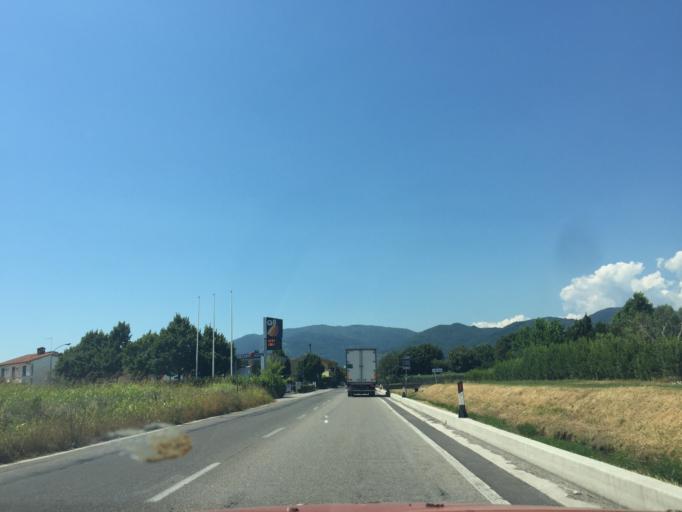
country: IT
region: Tuscany
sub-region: Provincia di Pistoia
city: Santa Lucia
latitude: 43.8699
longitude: 10.6970
